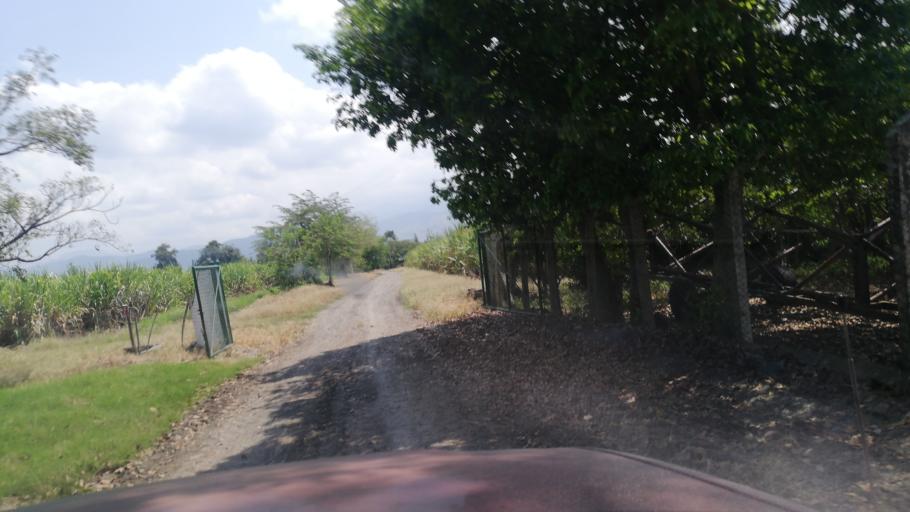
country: CO
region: Valle del Cauca
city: San Pedro
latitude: 3.9929
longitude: -76.2659
